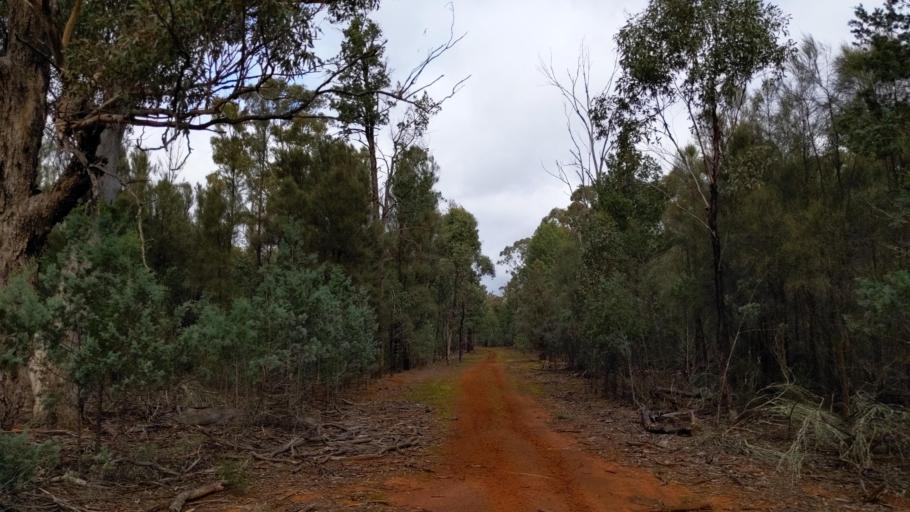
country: AU
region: New South Wales
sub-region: Coolamon
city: Coolamon
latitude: -34.8293
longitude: 146.9357
